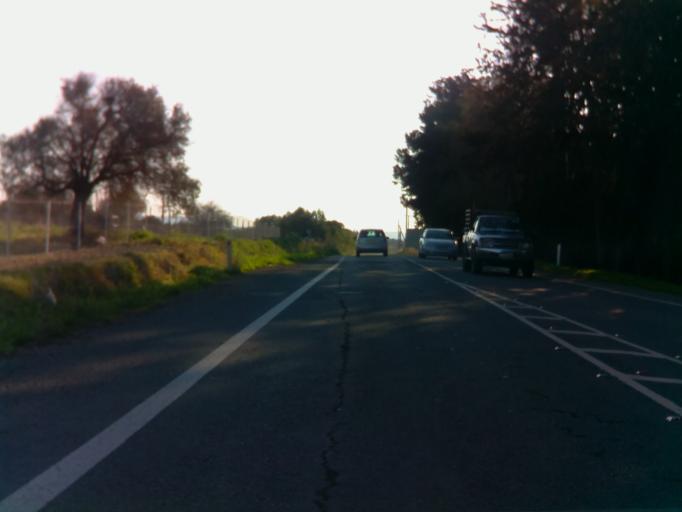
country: CY
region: Pafos
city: Paphos
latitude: 34.7339
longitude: 32.4982
